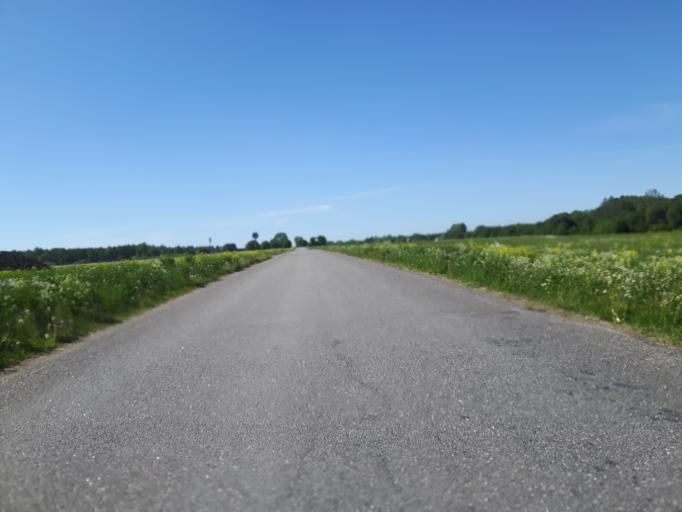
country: EE
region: Laeaene-Virumaa
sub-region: Haljala vald
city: Haljala
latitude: 59.5394
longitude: 26.2306
